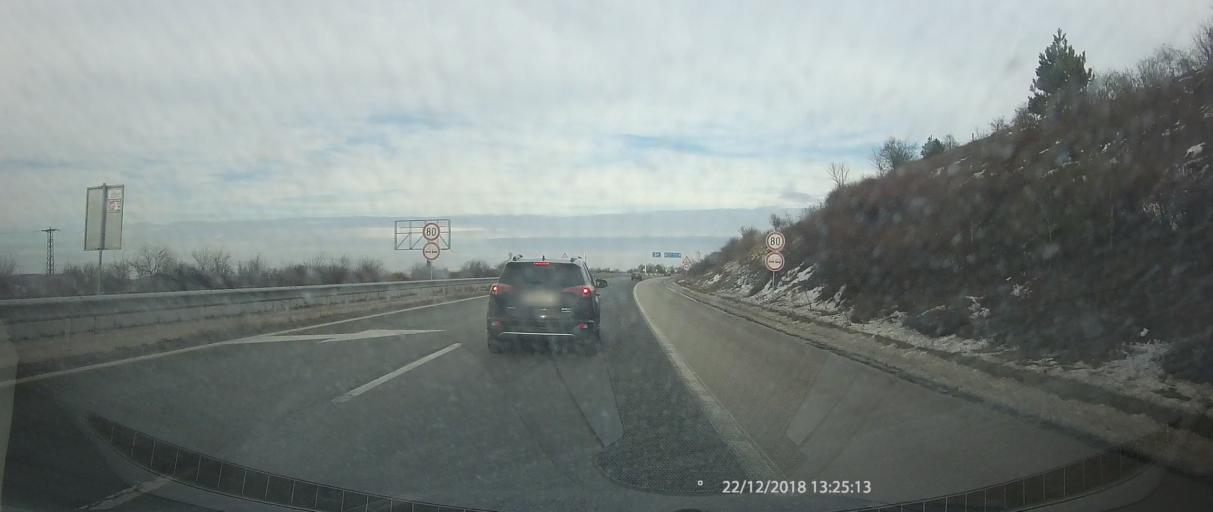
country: BG
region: Lovech
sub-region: Obshtina Yablanitsa
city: Yablanitsa
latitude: 43.0333
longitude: 24.1177
